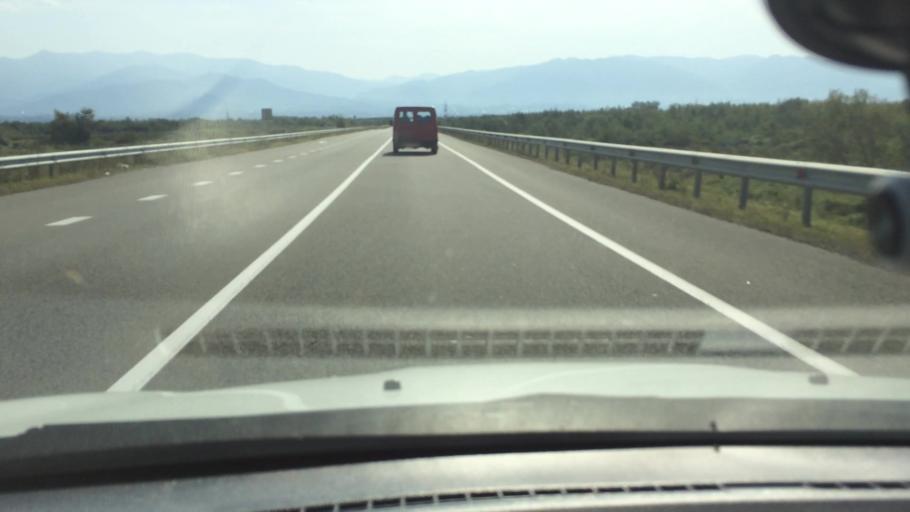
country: GE
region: Ajaria
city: Ochkhamuri
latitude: 41.8984
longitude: 41.7974
